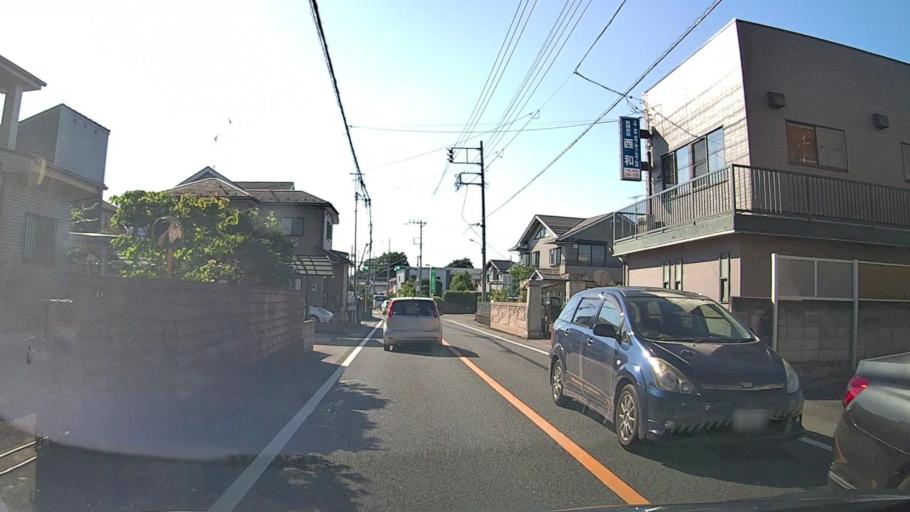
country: JP
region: Tokyo
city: Fussa
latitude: 35.7652
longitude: 139.3630
